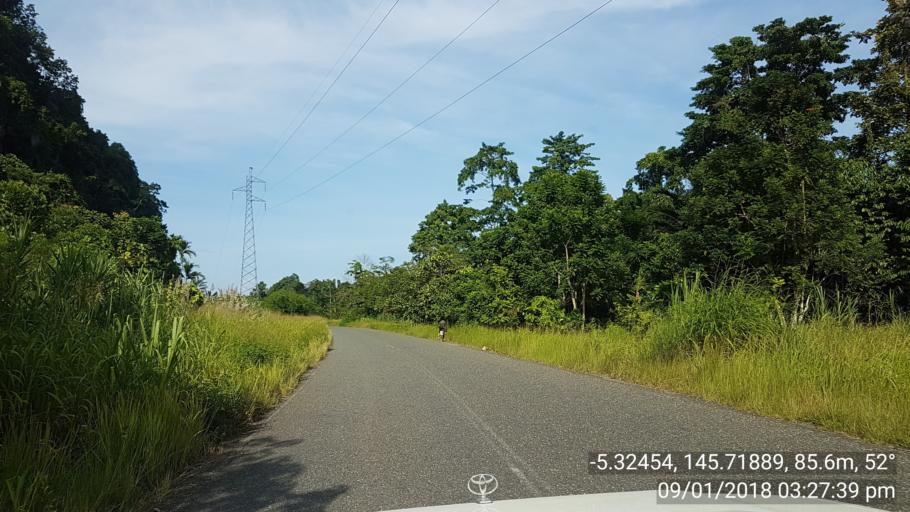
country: PG
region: Madang
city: Madang
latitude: -5.3244
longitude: 145.7189
